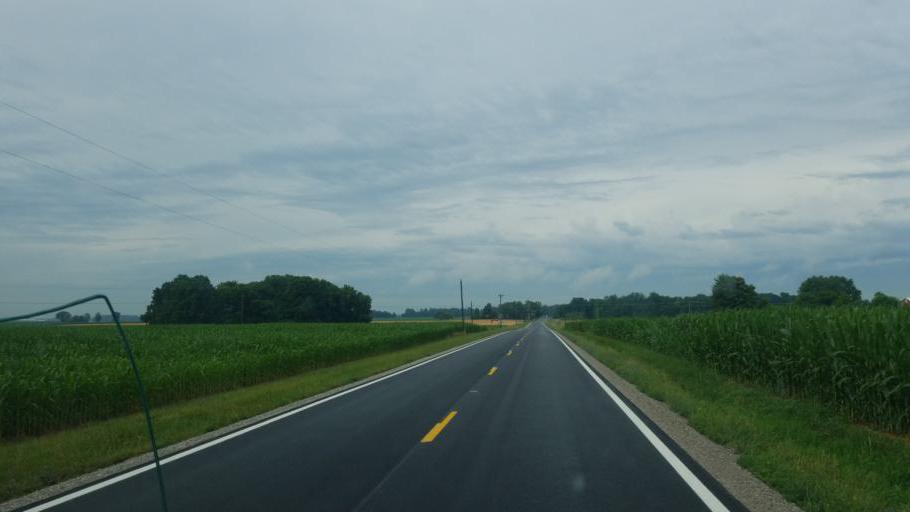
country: US
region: Ohio
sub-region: Defiance County
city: Hicksville
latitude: 41.3407
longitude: -84.6847
